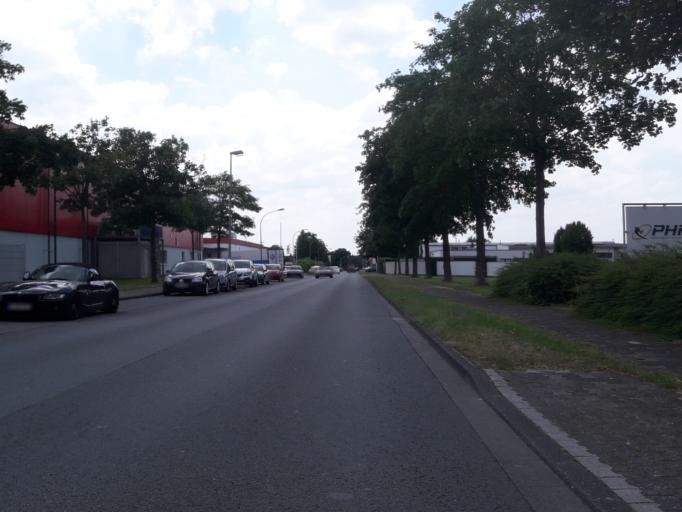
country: DE
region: North Rhine-Westphalia
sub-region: Regierungsbezirk Detmold
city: Paderborn
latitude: 51.7364
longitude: 8.7837
